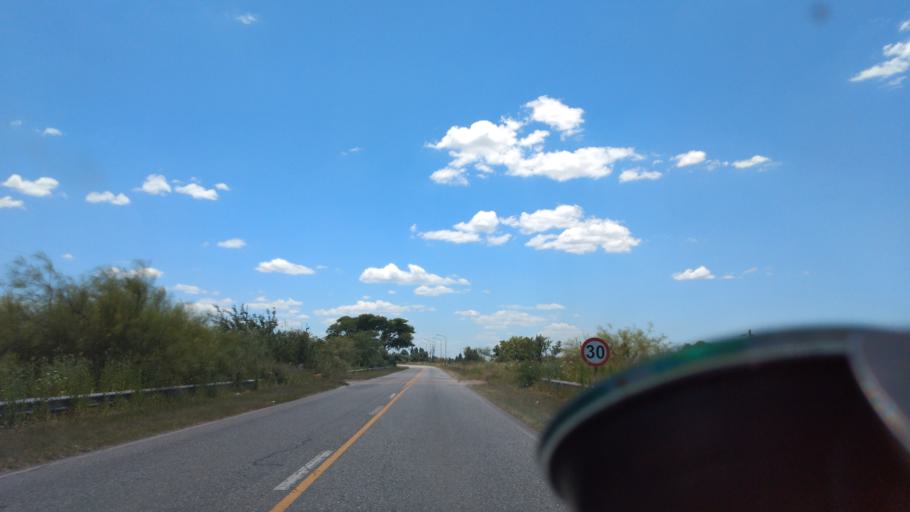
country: AR
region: Santa Fe
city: Laguna Paiva
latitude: -31.3302
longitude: -60.6596
